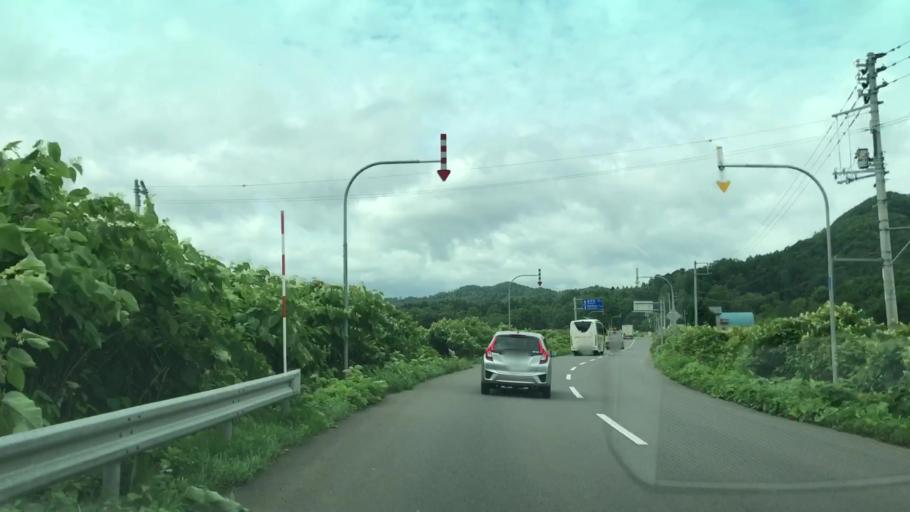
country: JP
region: Hokkaido
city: Niseko Town
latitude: 42.9490
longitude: 140.8290
